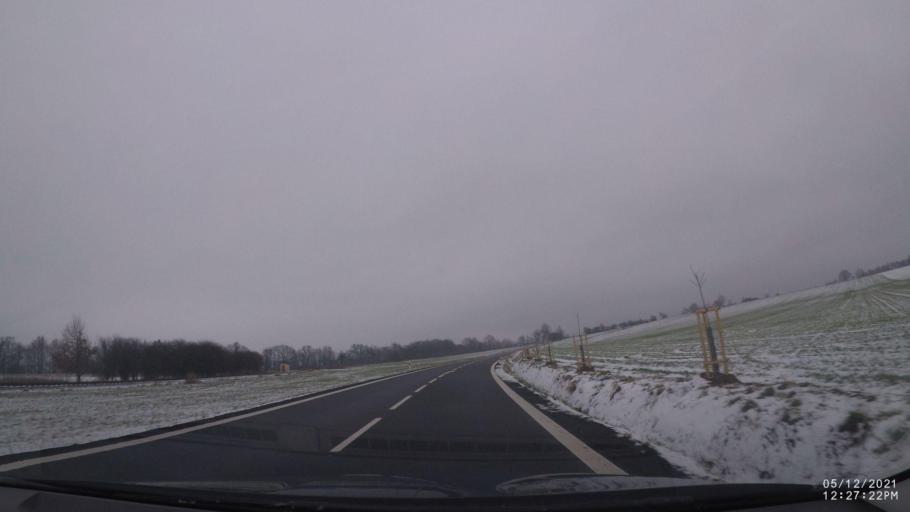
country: CZ
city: Nove Mesto nad Metuji
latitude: 50.3392
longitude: 16.1101
